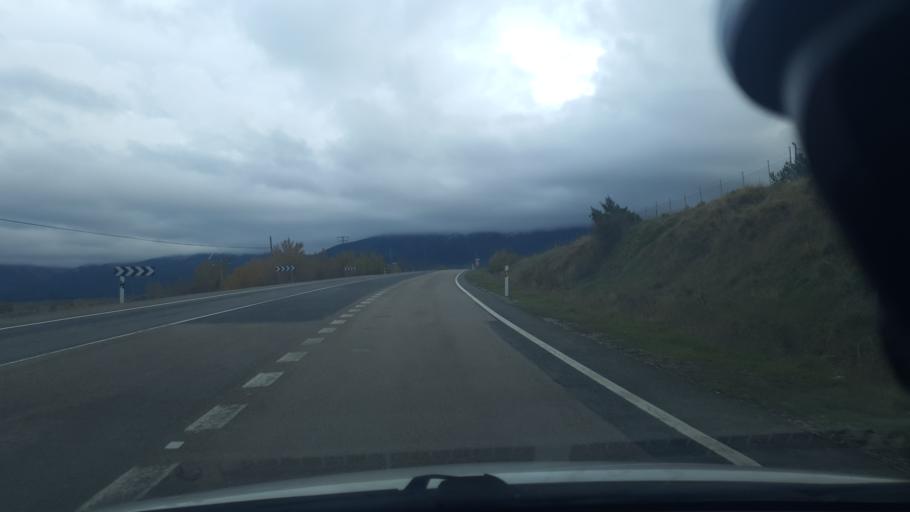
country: ES
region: Castille and Leon
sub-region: Provincia de Segovia
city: Cerezo de Abajo
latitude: 41.2151
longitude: -3.5875
